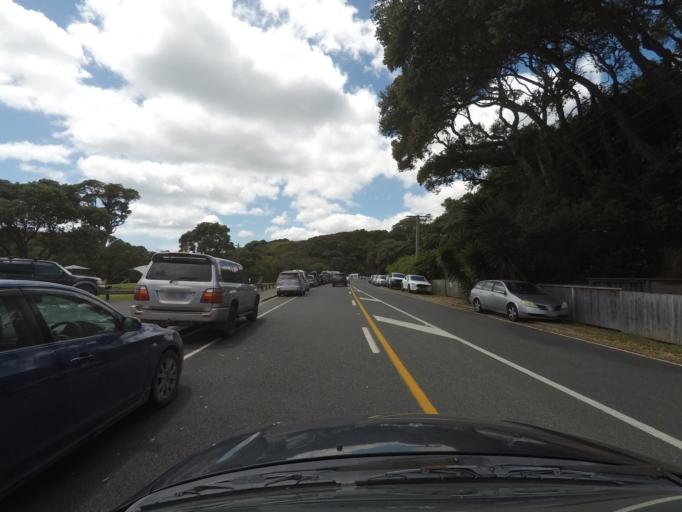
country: NZ
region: Northland
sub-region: Whangarei
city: Ruakaka
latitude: -36.0301
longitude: 174.5077
